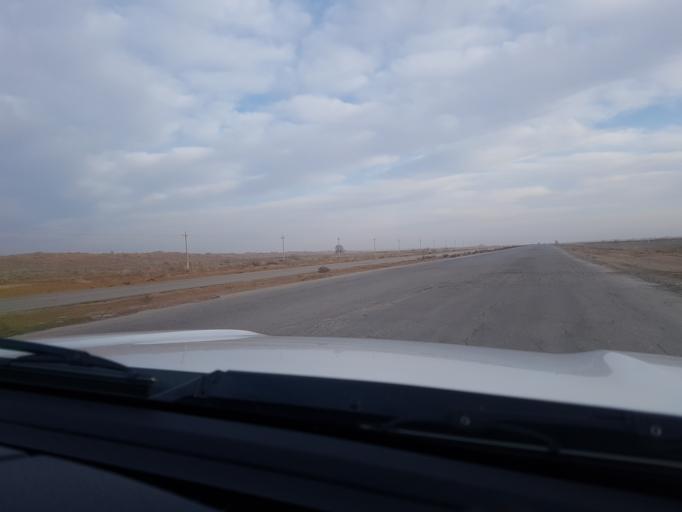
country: TM
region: Ahal
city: Abadan
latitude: 38.6031
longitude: 58.5012
